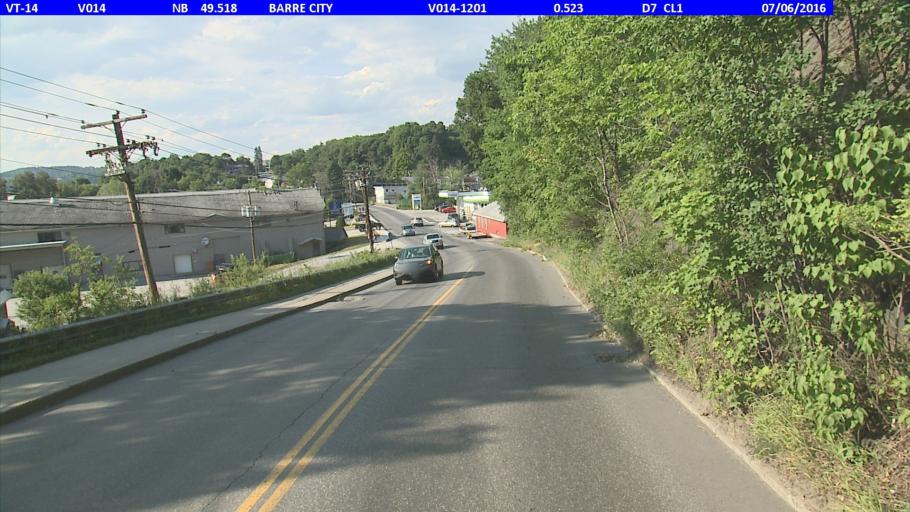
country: US
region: Vermont
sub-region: Washington County
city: Barre
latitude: 44.1883
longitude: -72.4986
